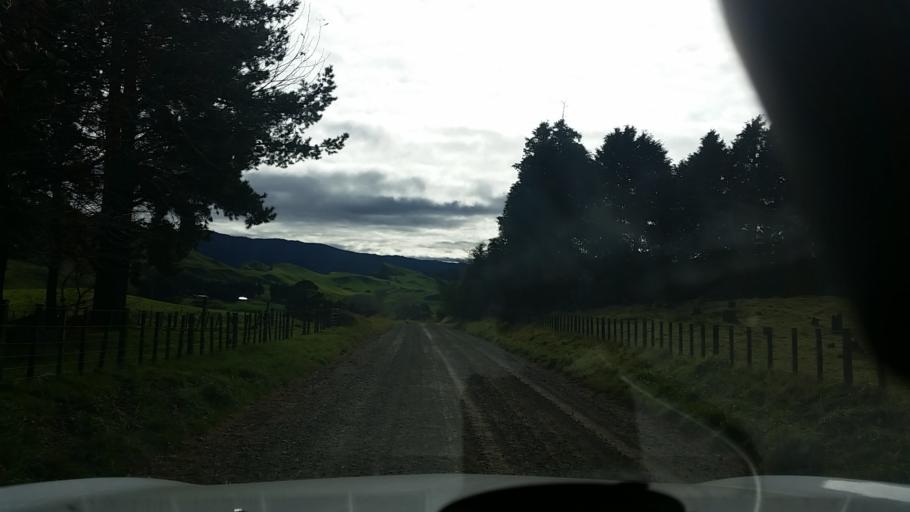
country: NZ
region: Hawke's Bay
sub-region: Napier City
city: Napier
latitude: -39.1322
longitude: 176.8958
